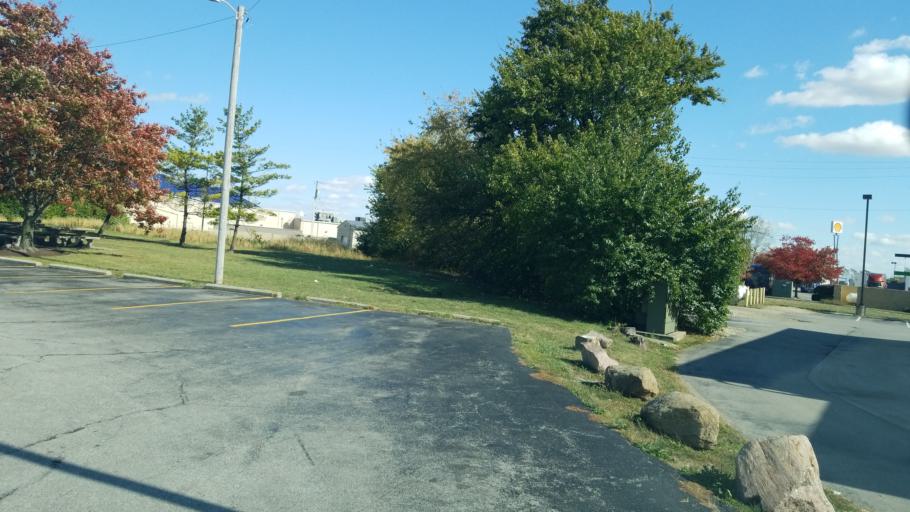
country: US
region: Ohio
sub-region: Fayette County
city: Jeffersonville
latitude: 39.6185
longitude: -83.6040
